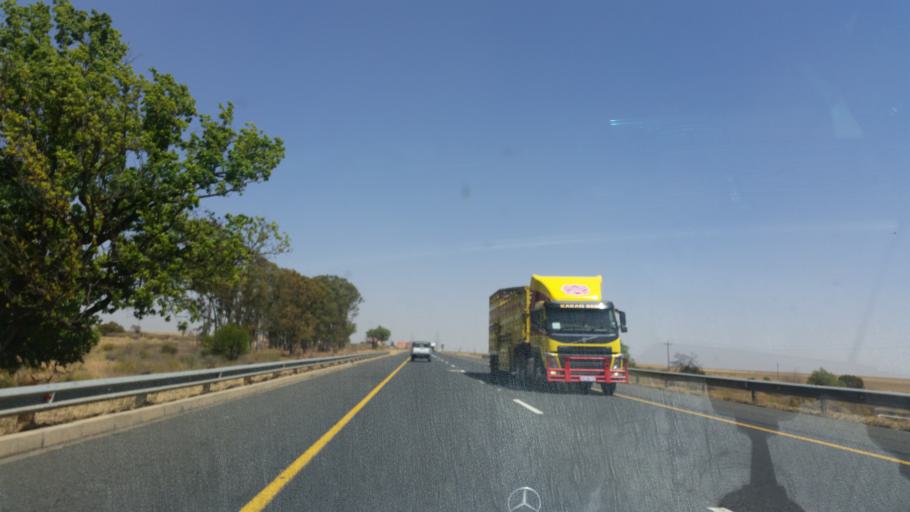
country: ZA
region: Orange Free State
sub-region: Lejweleputswa District Municipality
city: Brandfort
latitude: -28.7919
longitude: 26.6994
